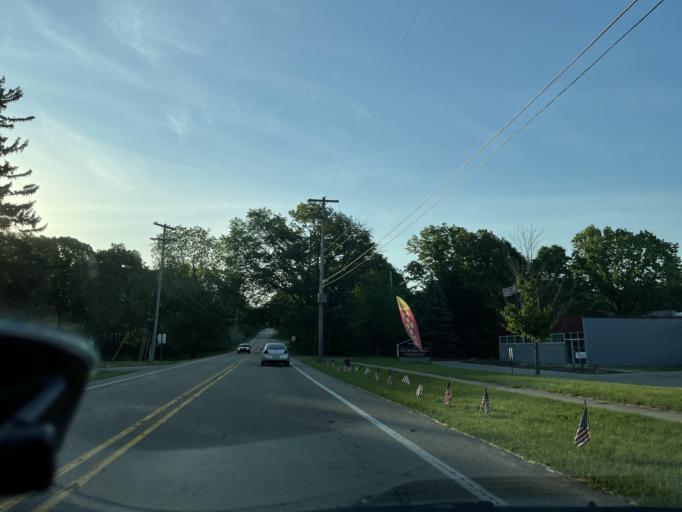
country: US
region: Michigan
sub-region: Barry County
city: Middleville
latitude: 42.7135
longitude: -85.4550
